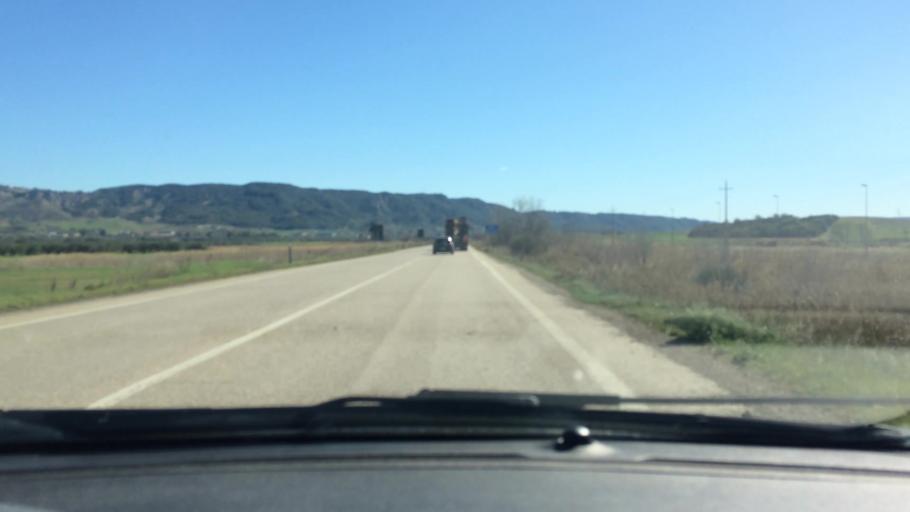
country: IT
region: Basilicate
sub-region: Provincia di Matera
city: Montescaglioso
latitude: 40.5315
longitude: 16.6147
